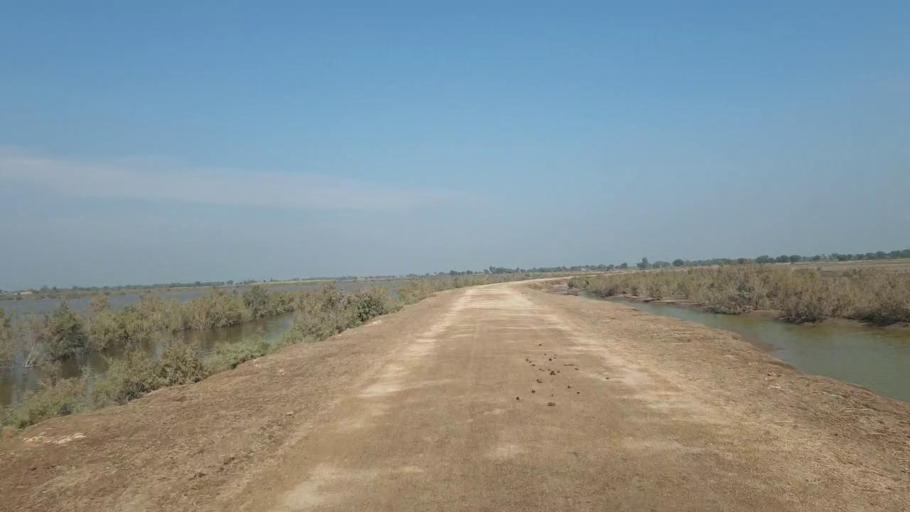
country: PK
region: Sindh
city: Shahdadpur
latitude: 25.9792
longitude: 68.5108
